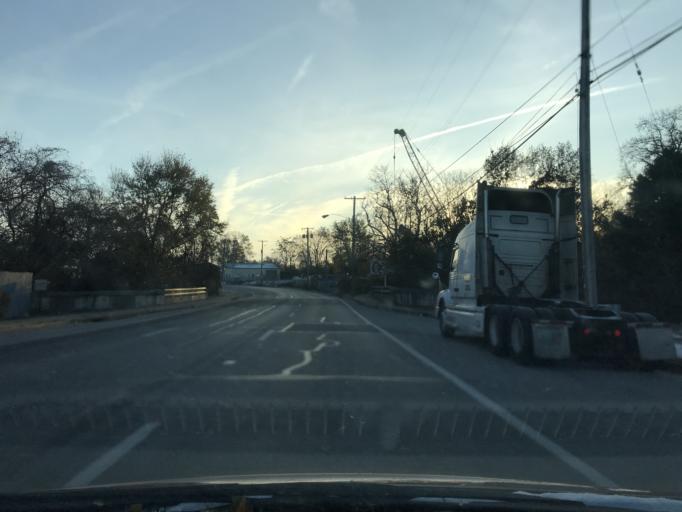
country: US
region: Indiana
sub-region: Clark County
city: Jeffersonville
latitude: 38.2535
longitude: -85.7281
